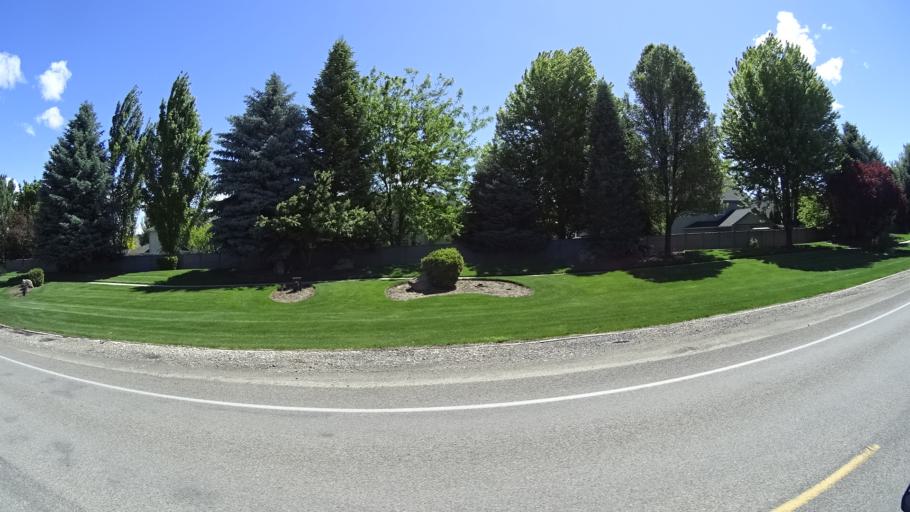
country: US
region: Idaho
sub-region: Ada County
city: Meridian
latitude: 43.6543
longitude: -116.3745
